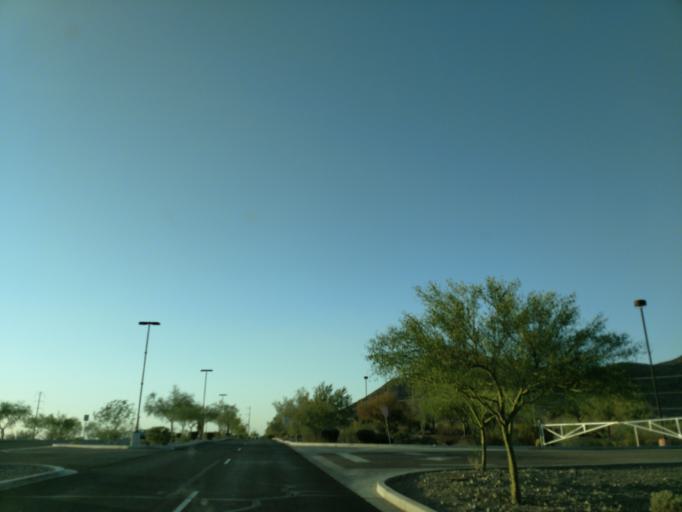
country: US
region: Arizona
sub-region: Maricopa County
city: Laveen
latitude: 33.3127
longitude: -112.1611
